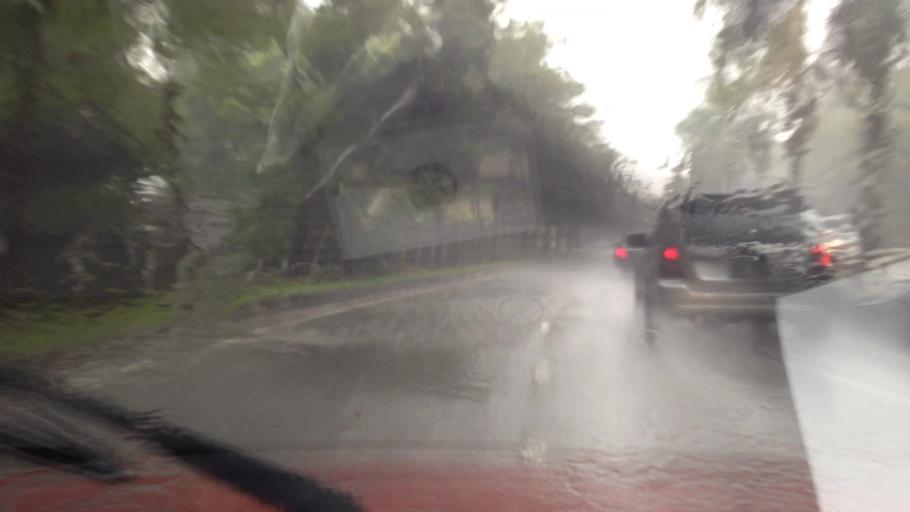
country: MY
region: Selangor
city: Subang Jaya
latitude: 3.0308
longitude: 101.5894
